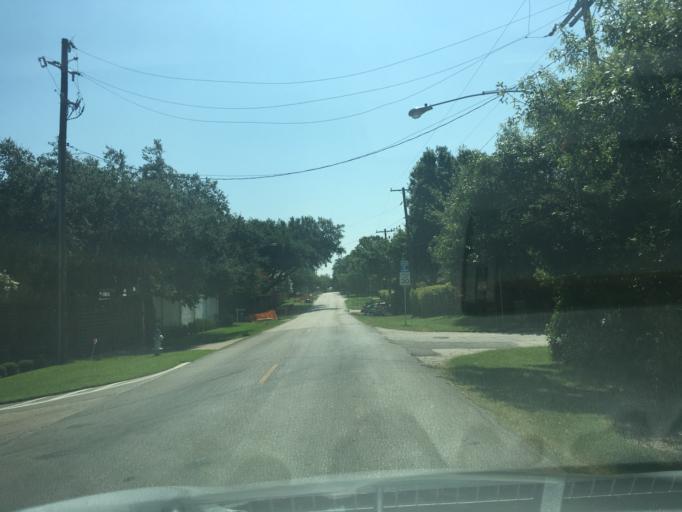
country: US
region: Texas
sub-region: Dallas County
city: Addison
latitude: 32.9134
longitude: -96.7964
